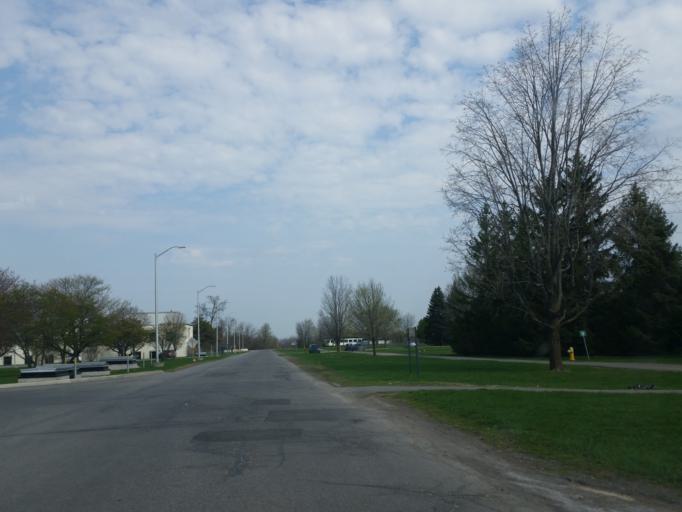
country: CA
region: Quebec
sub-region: Outaouais
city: Gatineau
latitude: 45.4531
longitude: -75.6219
